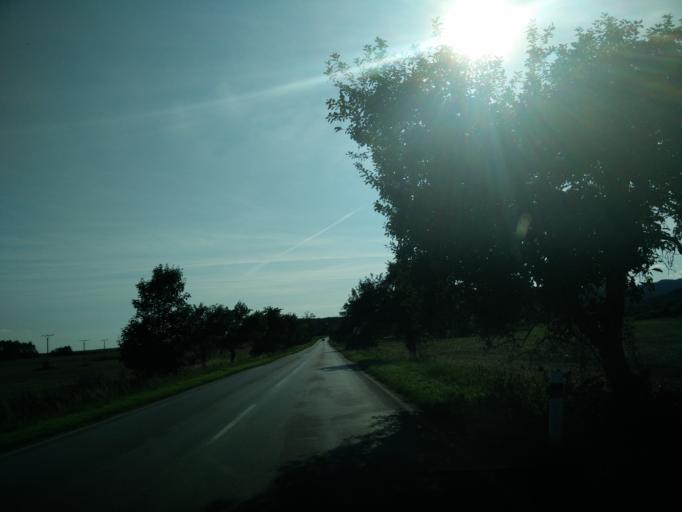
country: SK
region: Zilinsky
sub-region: Okres Martin
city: Martin
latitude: 48.9392
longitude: 18.8050
